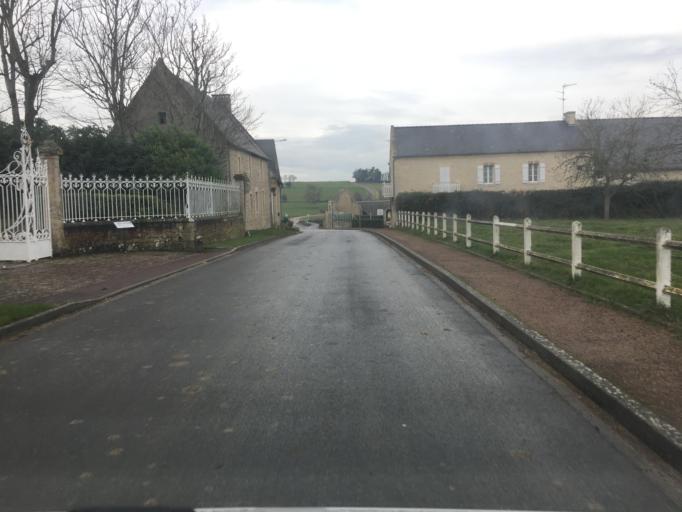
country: FR
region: Lower Normandy
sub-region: Departement du Calvados
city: Ver-sur-Mer
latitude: 49.3309
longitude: -0.6041
